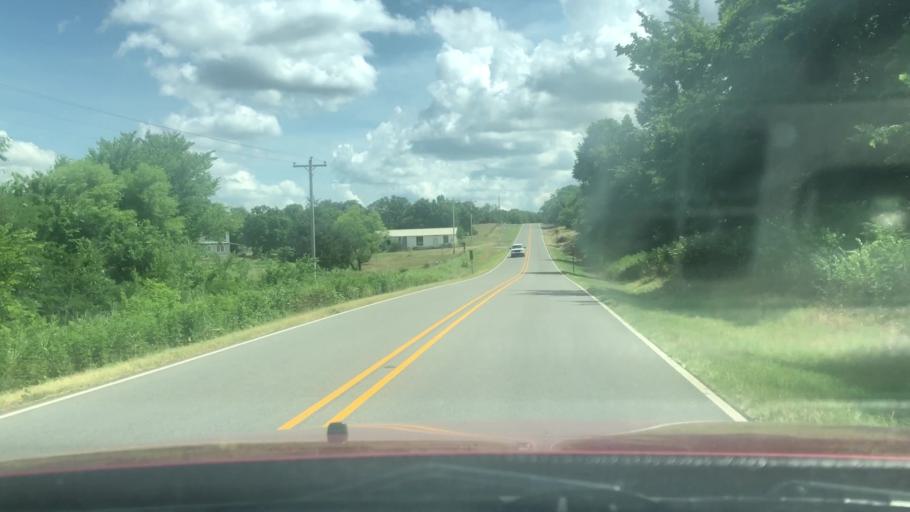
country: US
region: Arkansas
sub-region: Carroll County
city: Berryville
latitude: 36.4061
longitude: -93.5430
